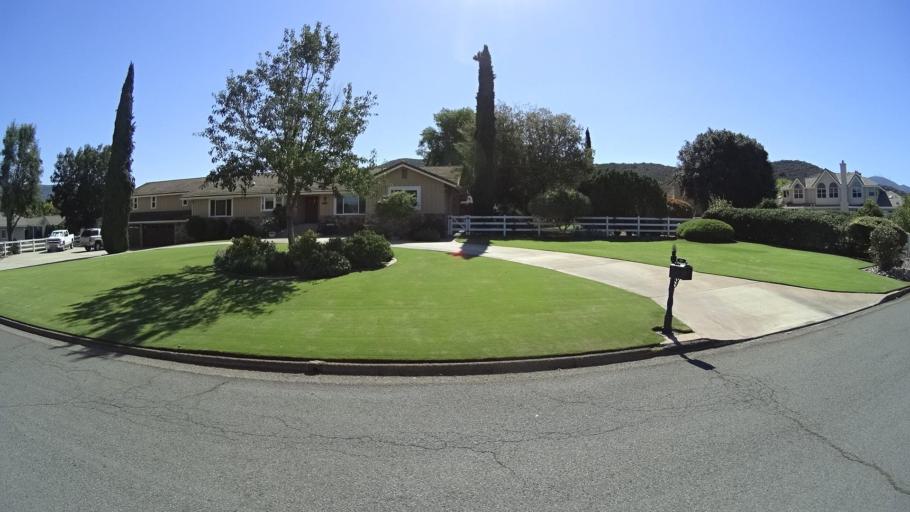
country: US
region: California
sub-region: San Diego County
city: Rancho San Diego
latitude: 32.7429
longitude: -116.9070
